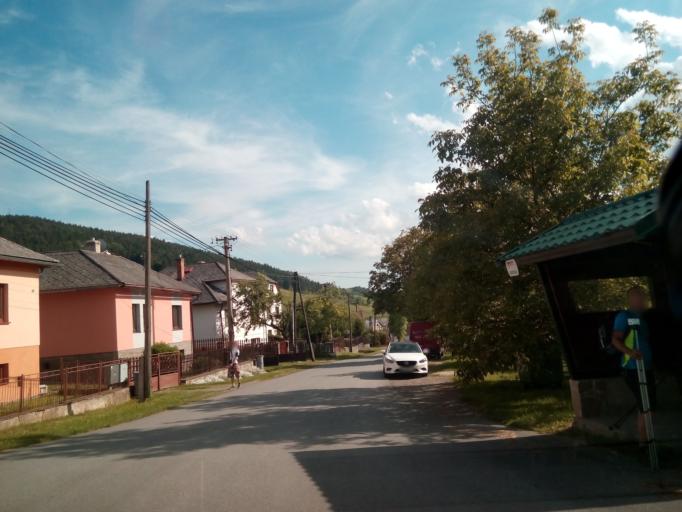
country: SK
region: Presovsky
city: Lipany
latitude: 49.0561
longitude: 20.9529
